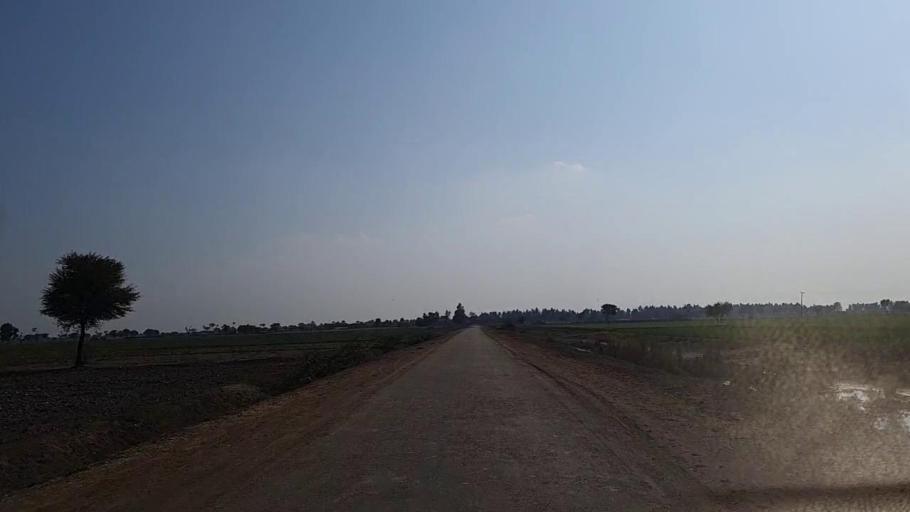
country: PK
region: Sindh
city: Jam Sahib
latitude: 26.2814
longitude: 68.5828
